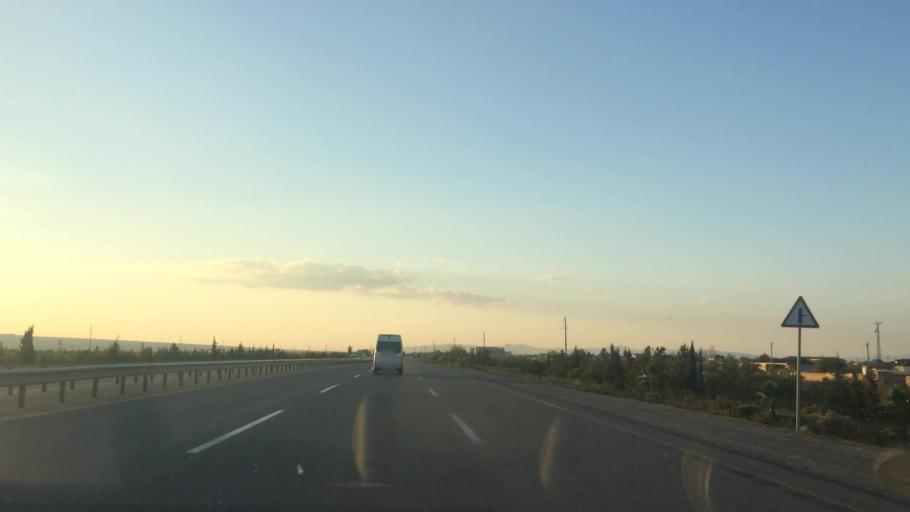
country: AZ
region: Haciqabul
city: Haciqabul
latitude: 40.0036
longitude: 49.1659
